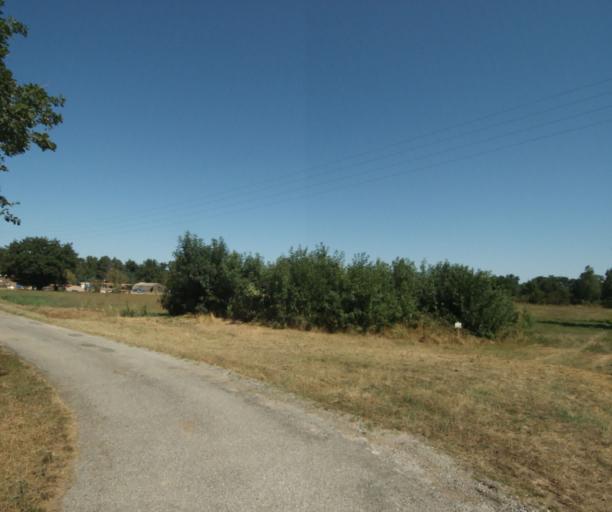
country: FR
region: Midi-Pyrenees
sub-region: Departement de la Haute-Garonne
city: Revel
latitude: 43.4746
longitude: 1.9856
